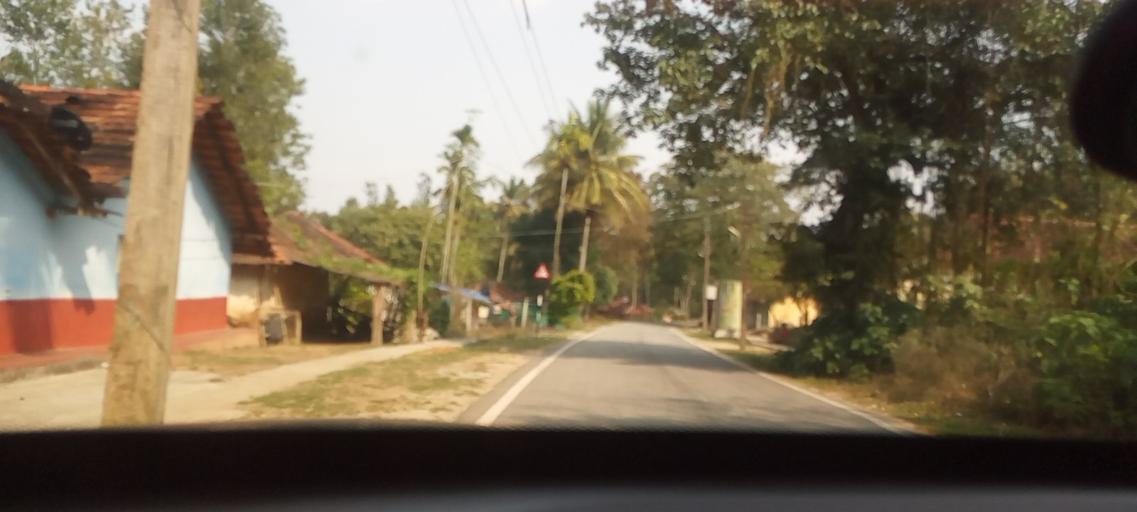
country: IN
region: Karnataka
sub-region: Hassan
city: Belur
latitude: 13.1896
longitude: 75.7923
